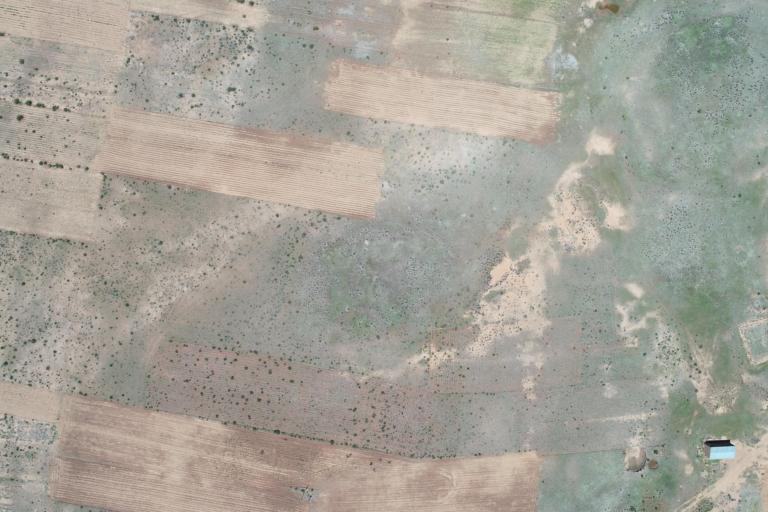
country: BO
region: La Paz
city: Patacamaya
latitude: -17.2754
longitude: -68.5120
